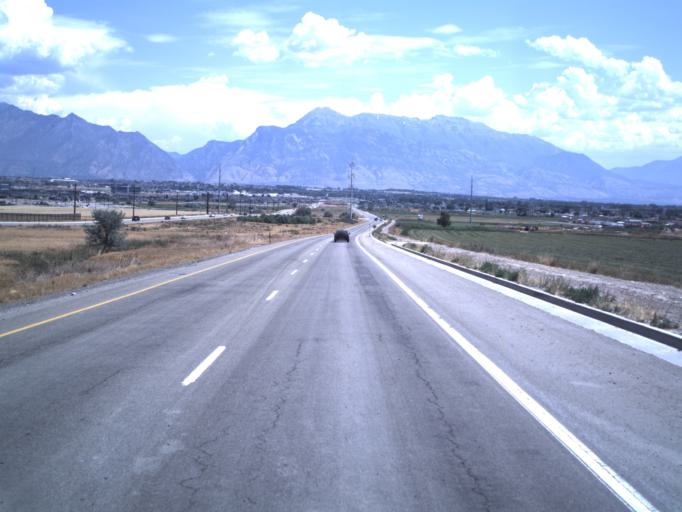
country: US
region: Utah
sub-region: Utah County
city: Saratoga Springs
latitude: 40.4126
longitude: -111.9165
